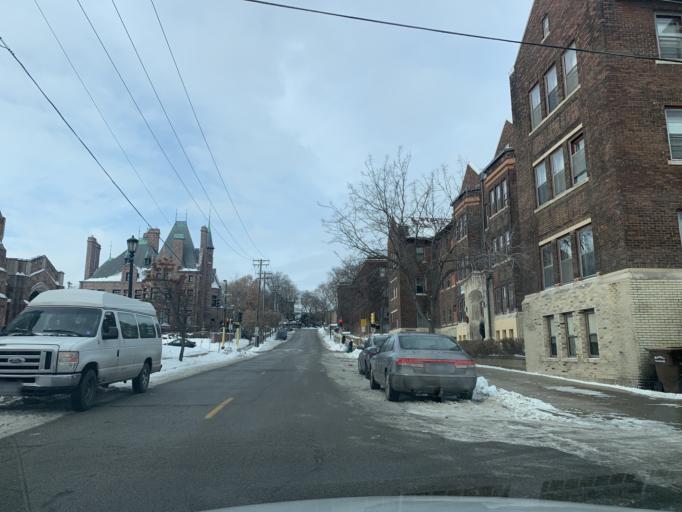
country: US
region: Minnesota
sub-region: Hennepin County
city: Minneapolis
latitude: 44.9642
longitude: -93.2785
